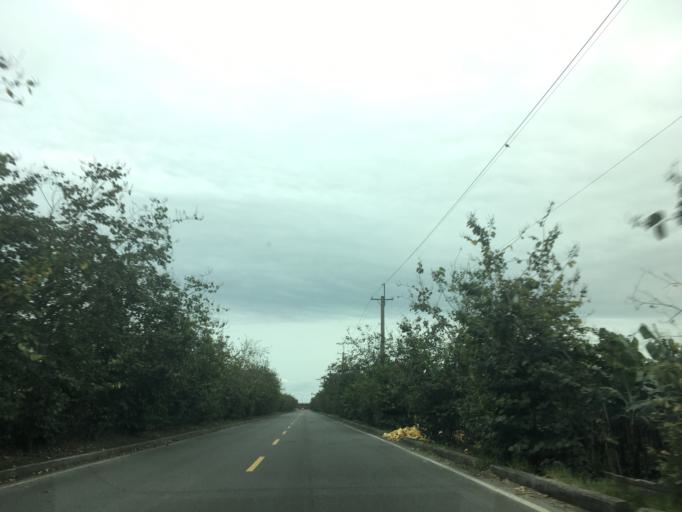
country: TW
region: Taiwan
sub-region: Taitung
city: Taitung
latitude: 22.7962
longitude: 121.1373
